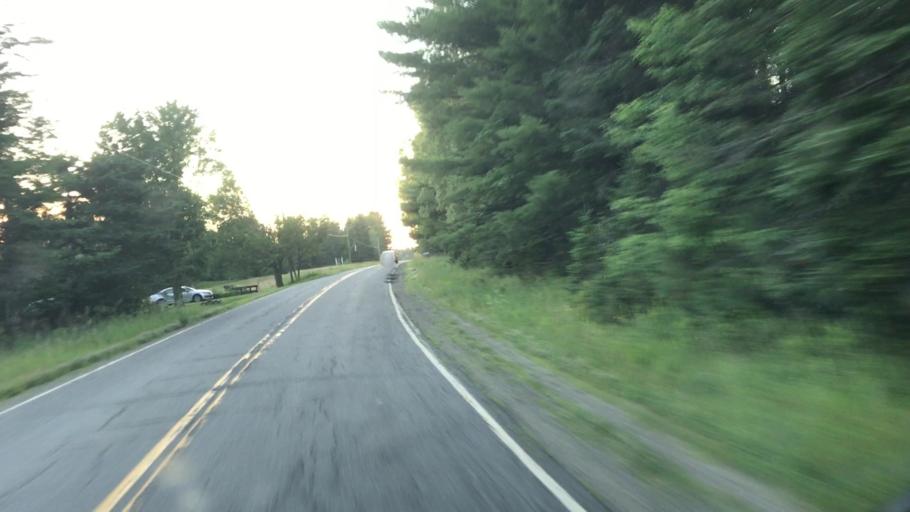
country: US
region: Maine
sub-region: Penobscot County
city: Medway
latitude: 45.5980
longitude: -68.2458
